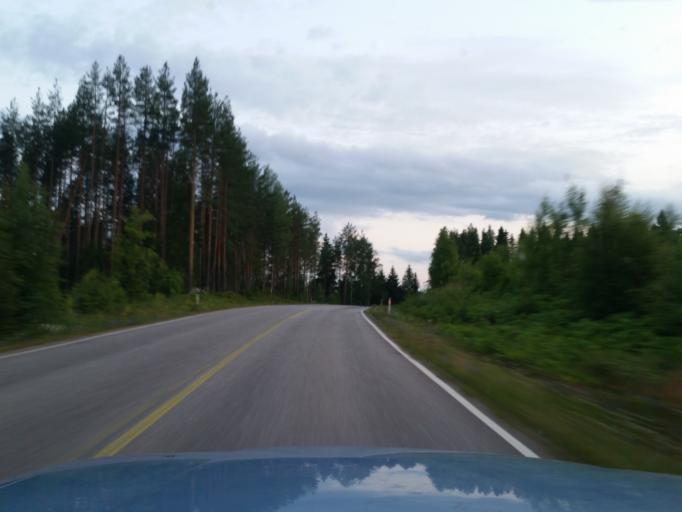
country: FI
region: Southern Savonia
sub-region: Savonlinna
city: Sulkava
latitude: 61.8102
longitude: 28.4271
